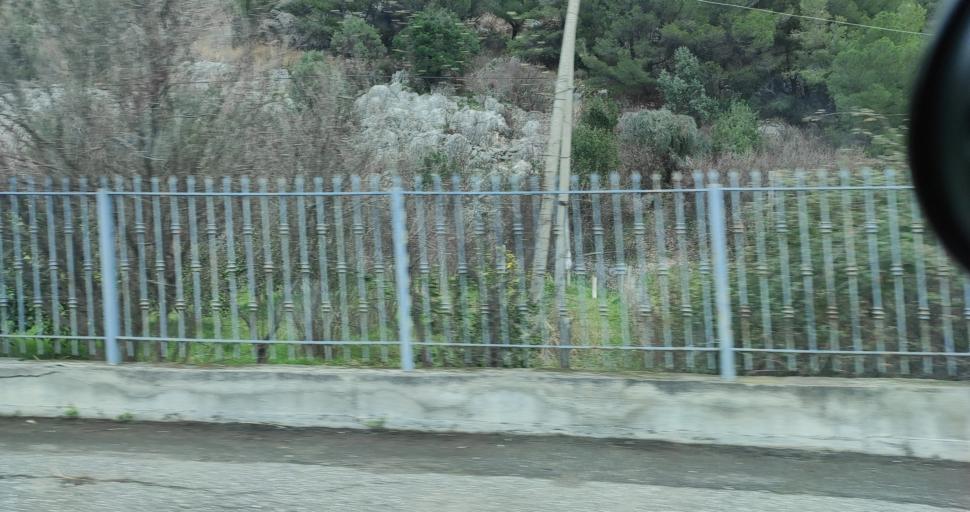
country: AL
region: Lezhe
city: Lezhe
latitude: 41.7933
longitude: 19.6221
